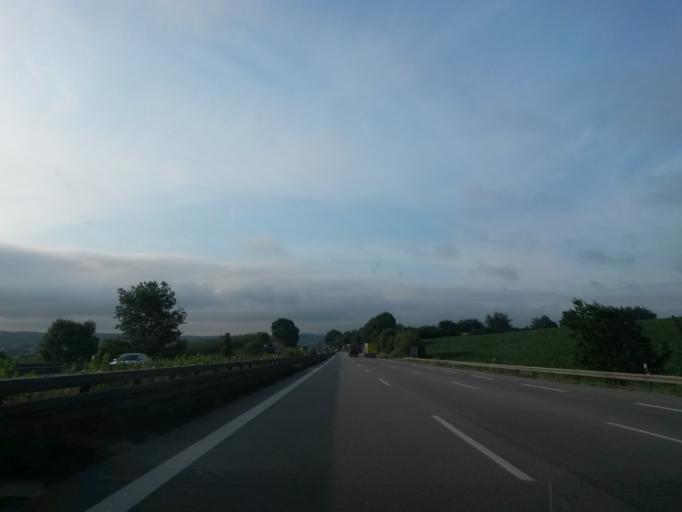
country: DE
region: Bavaria
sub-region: Upper Bavaria
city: Rohrbach
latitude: 48.6092
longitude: 11.5442
